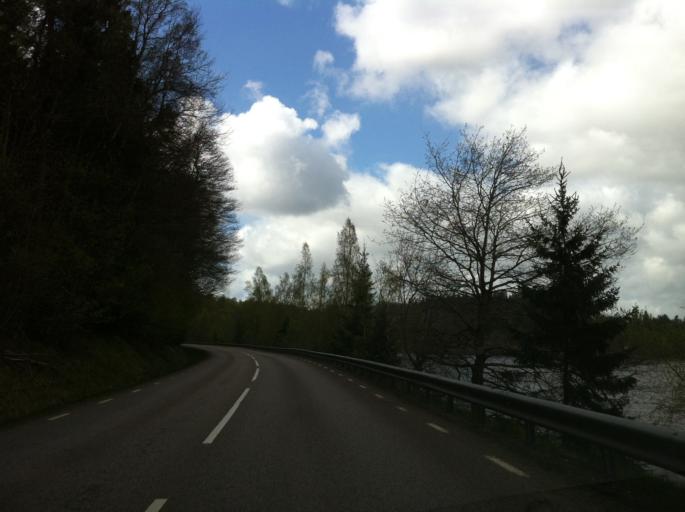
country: SE
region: Vaestra Goetaland
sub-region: Alingsas Kommun
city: Alingsas
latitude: 57.8563
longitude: 12.5461
